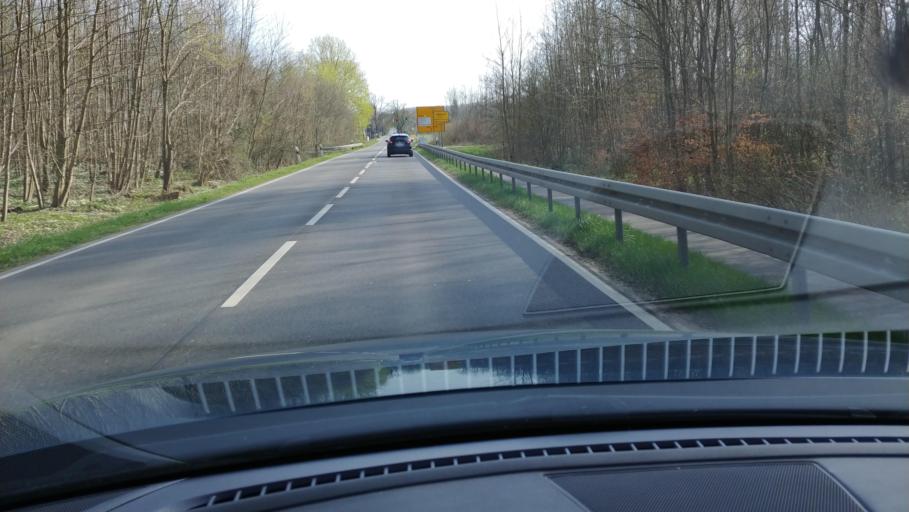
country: DE
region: Mecklenburg-Vorpommern
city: Lubstorf
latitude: 53.7321
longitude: 11.4048
